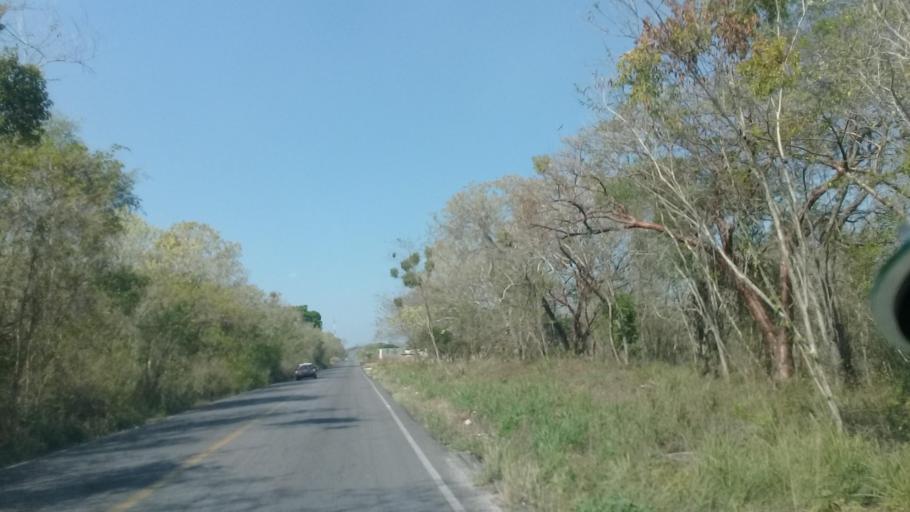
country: MX
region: Veracruz
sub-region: Emiliano Zapata
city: Plan del Rio
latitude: 19.4043
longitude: -96.6136
